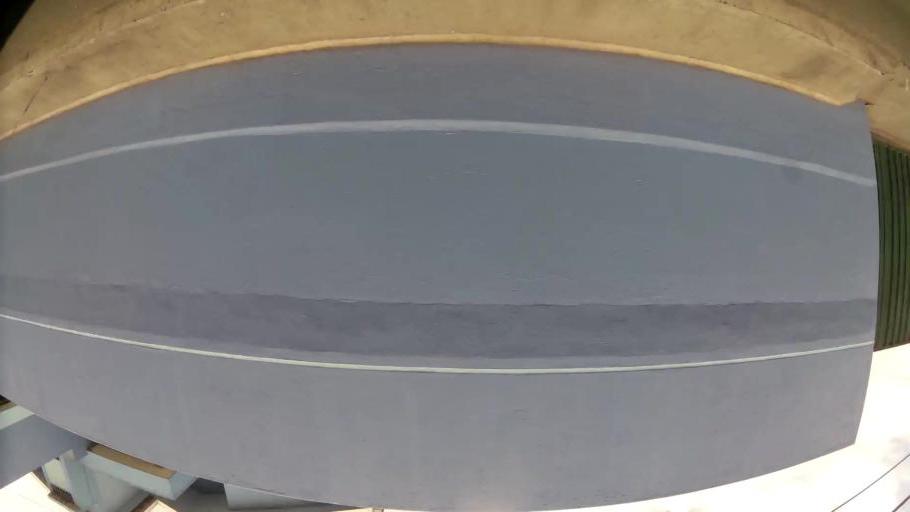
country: EC
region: Pichincha
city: Quito
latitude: -0.0808
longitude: -78.4177
